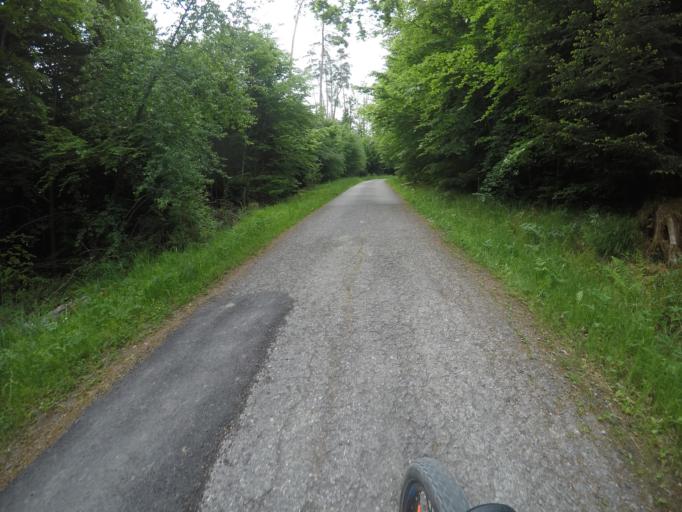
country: DE
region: Baden-Wuerttemberg
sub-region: Regierungsbezirk Stuttgart
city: Schlaitdorf
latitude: 48.6022
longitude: 9.1754
